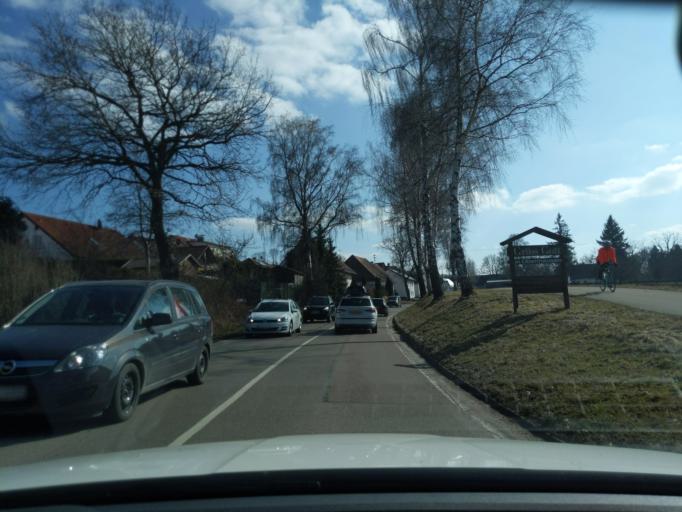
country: DE
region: Bavaria
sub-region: Swabia
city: Buch
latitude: 48.2403
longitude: 10.1751
